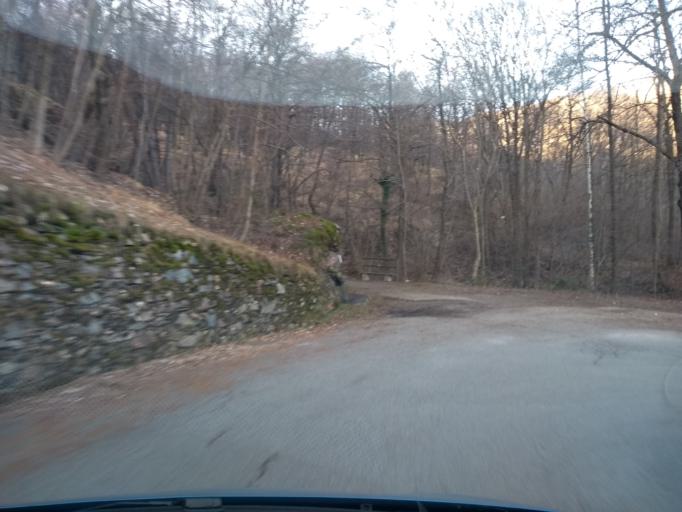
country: IT
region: Piedmont
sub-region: Provincia di Torino
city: Coassolo Torinese
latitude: 45.2826
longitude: 7.4566
